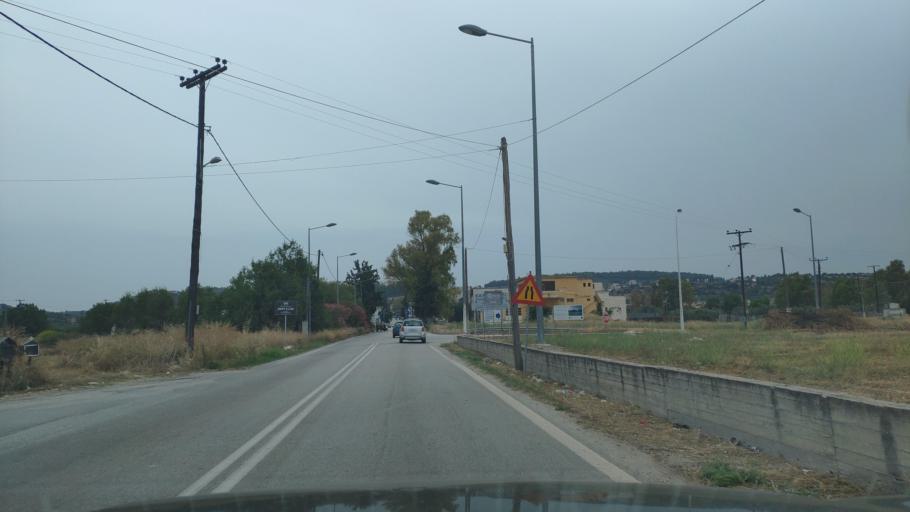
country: GR
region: Peloponnese
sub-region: Nomos Argolidos
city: Kranidi
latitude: 37.3957
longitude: 23.1567
